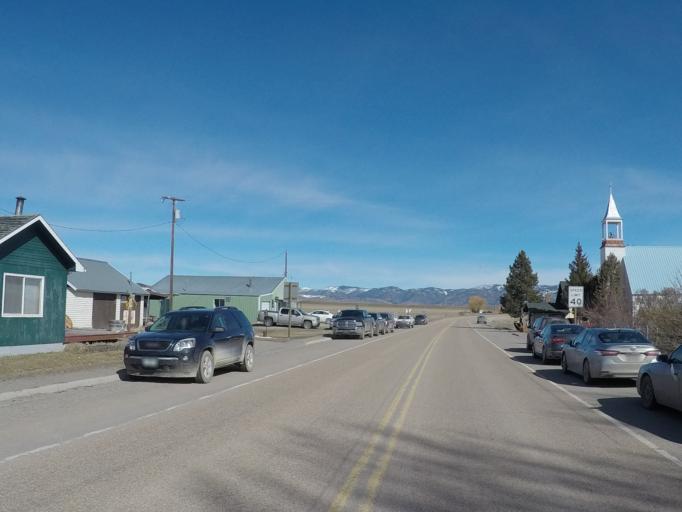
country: US
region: Montana
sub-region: Granite County
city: Philipsburg
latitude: 46.5869
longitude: -113.1964
